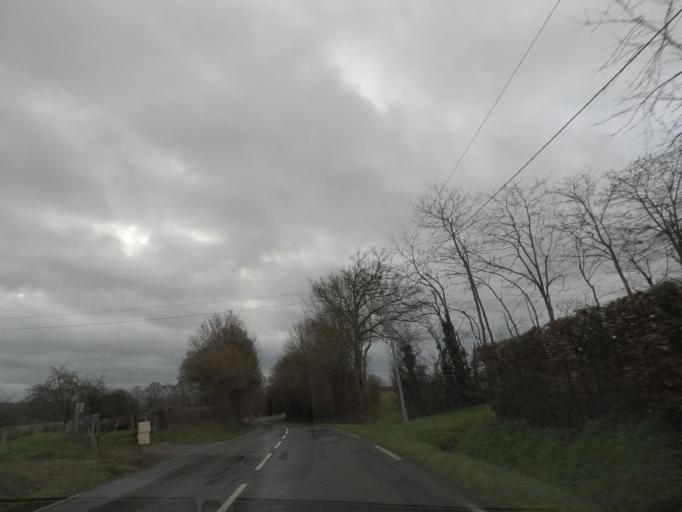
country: FR
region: Pays de la Loire
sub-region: Departement de la Sarthe
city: La Ferte-Bernard
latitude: 48.2087
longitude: 0.6317
